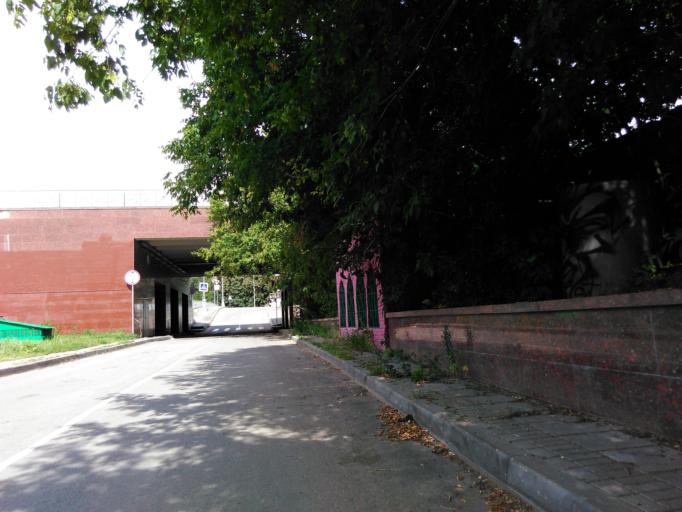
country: RU
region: Moscow
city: Novyye Cheremushki
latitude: 55.7120
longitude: 37.5779
